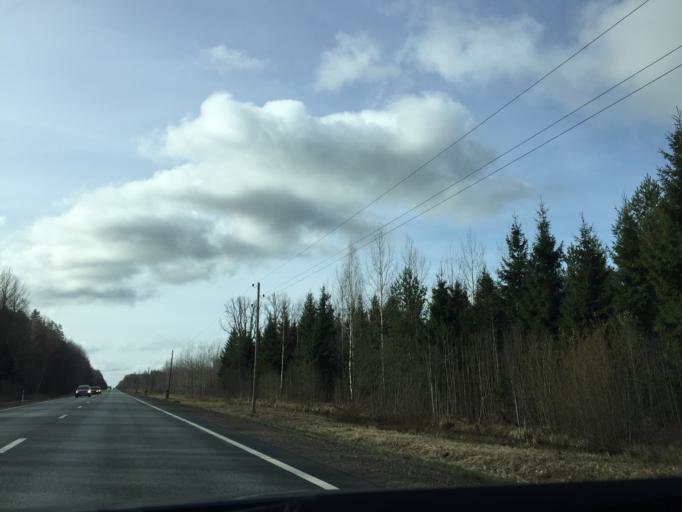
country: LV
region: Jelgava
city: Jelgava
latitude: 56.5660
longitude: 23.7128
